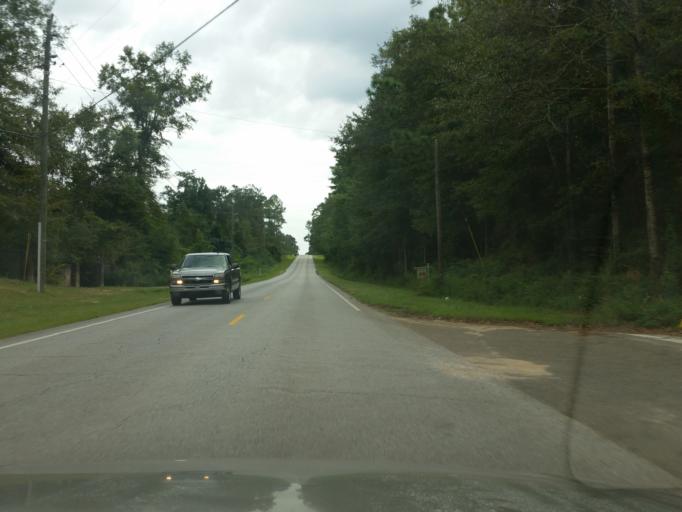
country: US
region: Florida
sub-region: Escambia County
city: Molino
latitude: 30.7080
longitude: -87.3351
